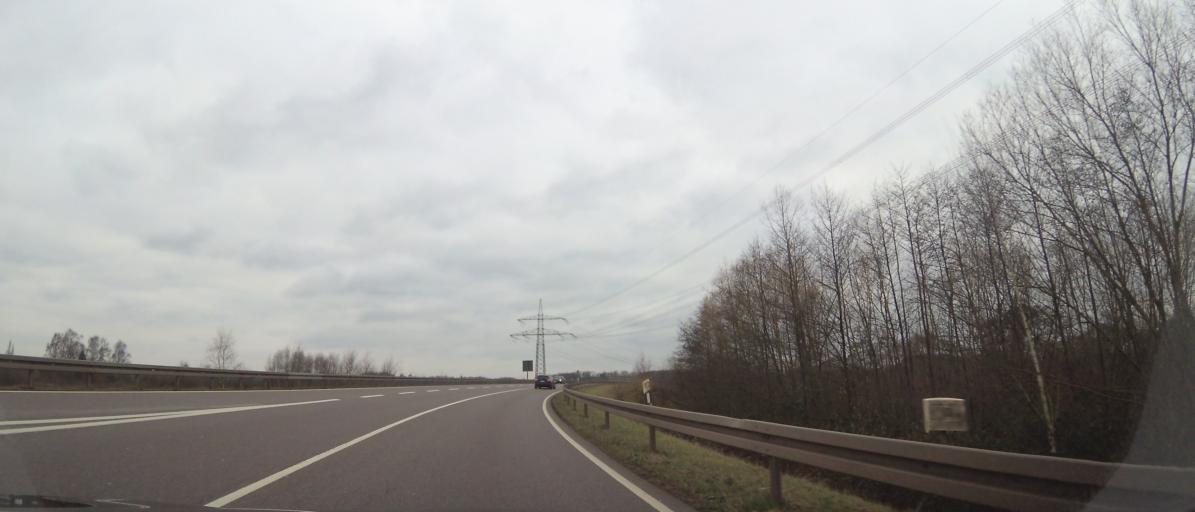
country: DE
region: Saarland
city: Ensdorf
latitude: 49.2876
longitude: 6.7785
